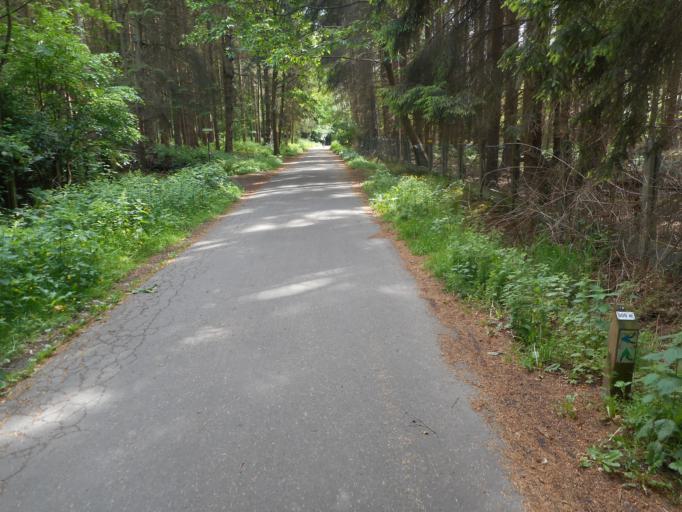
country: BE
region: Flanders
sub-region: Provincie Oost-Vlaanderen
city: Waasmunster
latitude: 51.1526
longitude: 4.0711
